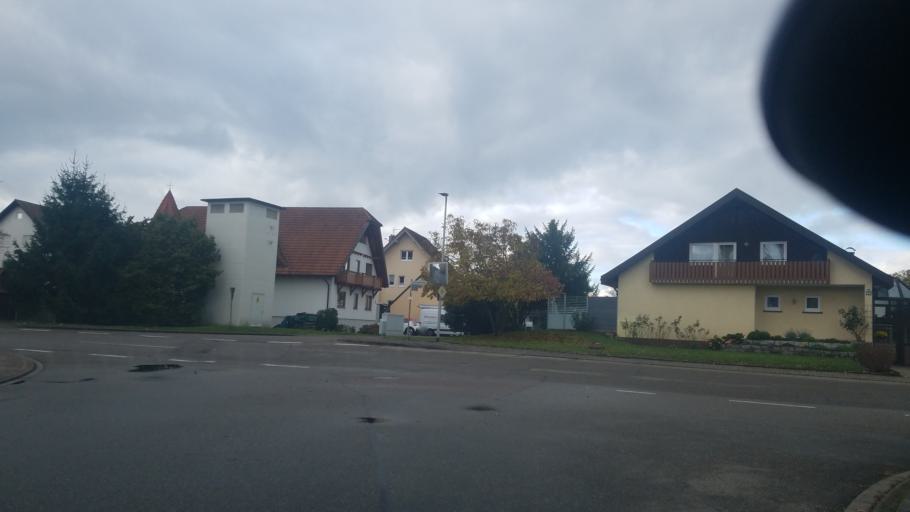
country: DE
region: Baden-Wuerttemberg
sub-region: Karlsruhe Region
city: Zell
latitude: 48.6546
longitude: 8.0251
